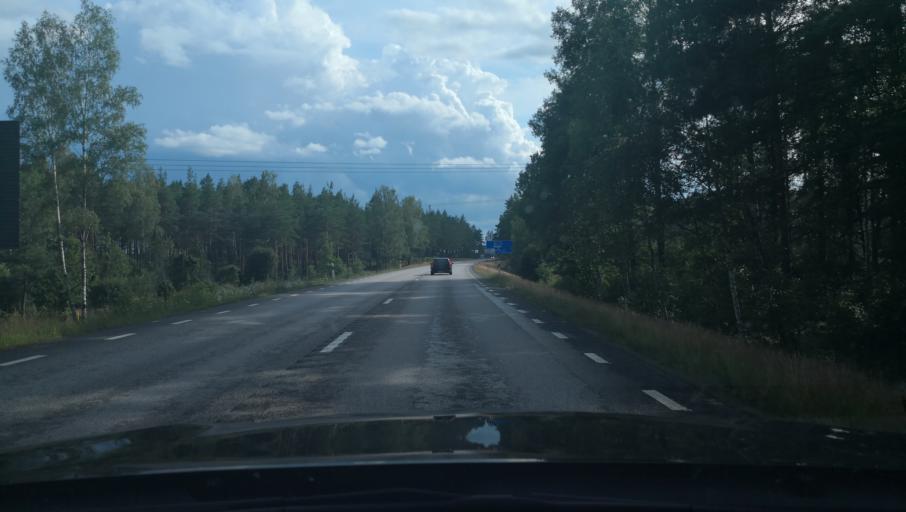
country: SE
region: Kalmar
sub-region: Hultsfreds Kommun
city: Hultsfred
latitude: 57.5145
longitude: 15.8405
